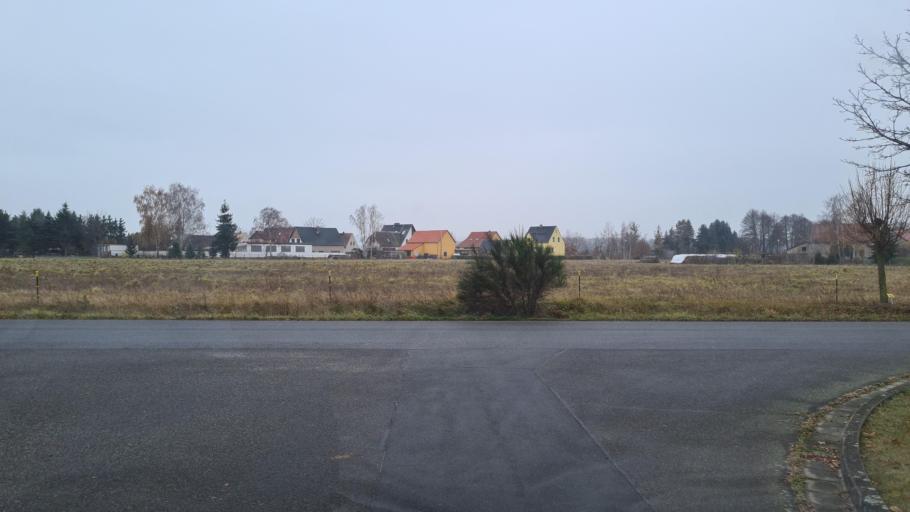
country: DE
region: Brandenburg
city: Lindenau
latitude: 51.4005
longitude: 13.7299
